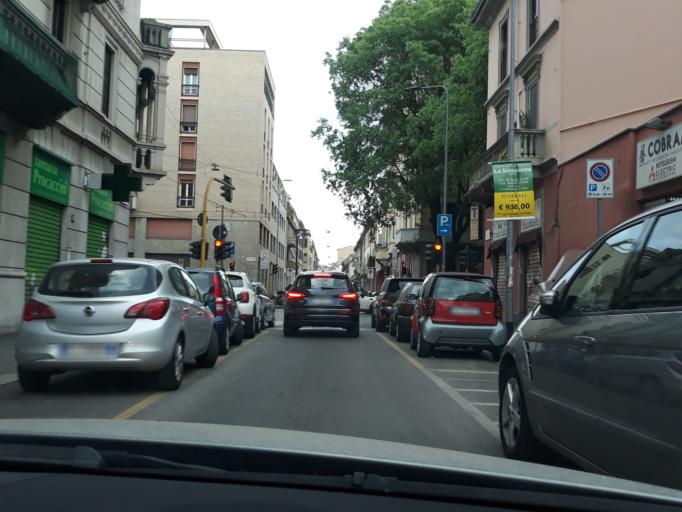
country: IT
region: Lombardy
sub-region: Citta metropolitana di Milano
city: Milano
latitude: 45.4840
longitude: 9.1703
